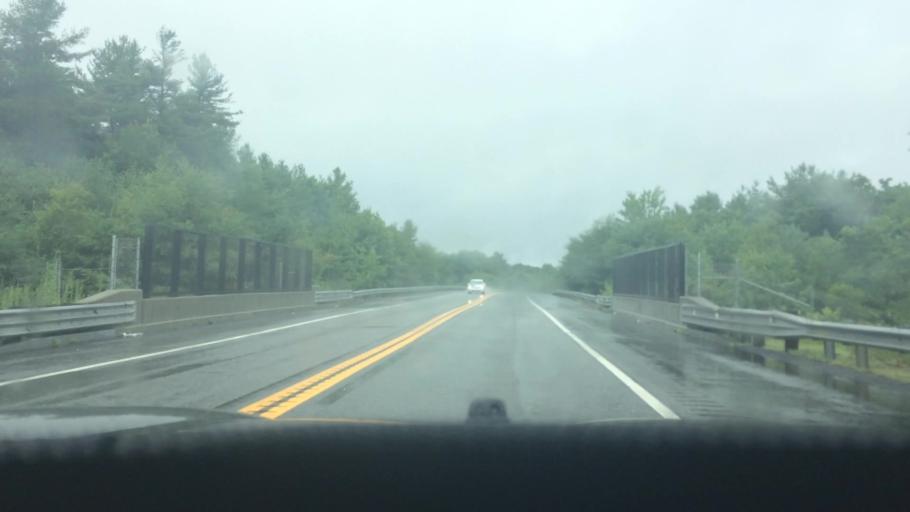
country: US
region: Massachusetts
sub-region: Worcester County
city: South Ashburnham
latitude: 42.5741
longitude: -71.9481
